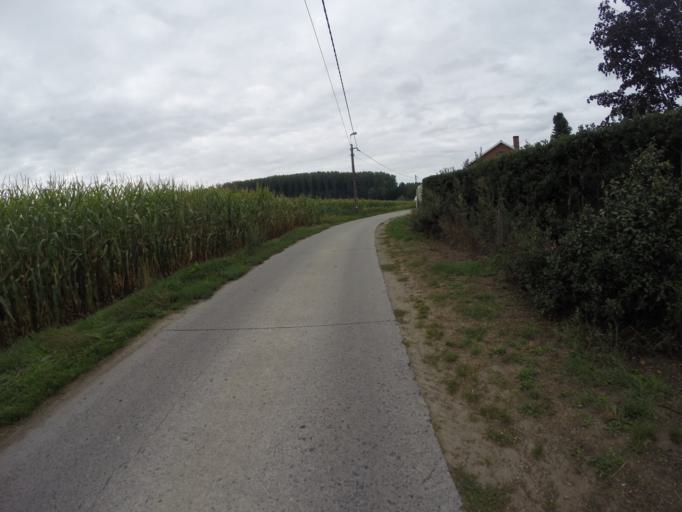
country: BE
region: Flanders
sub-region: Provincie Oost-Vlaanderen
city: Aalter
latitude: 51.0597
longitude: 3.4305
